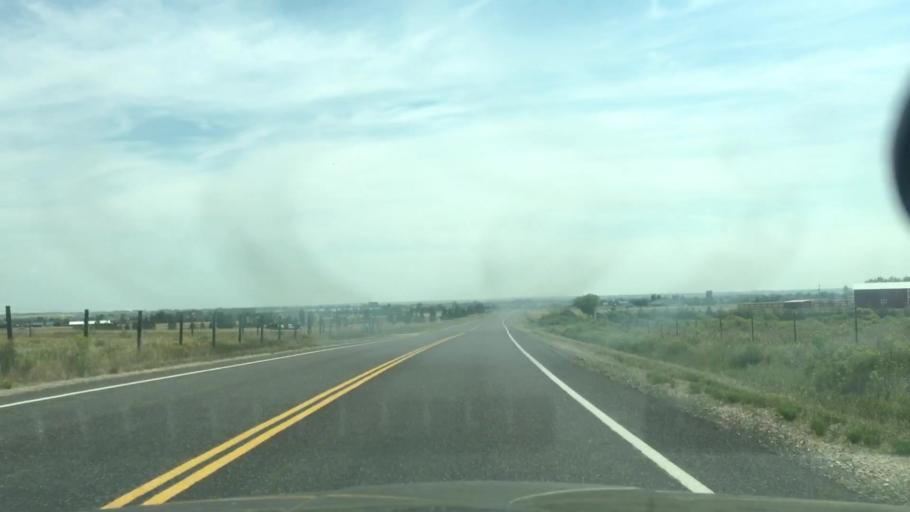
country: US
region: Colorado
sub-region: Larimer County
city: Berthoud
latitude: 40.3363
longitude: -105.1706
